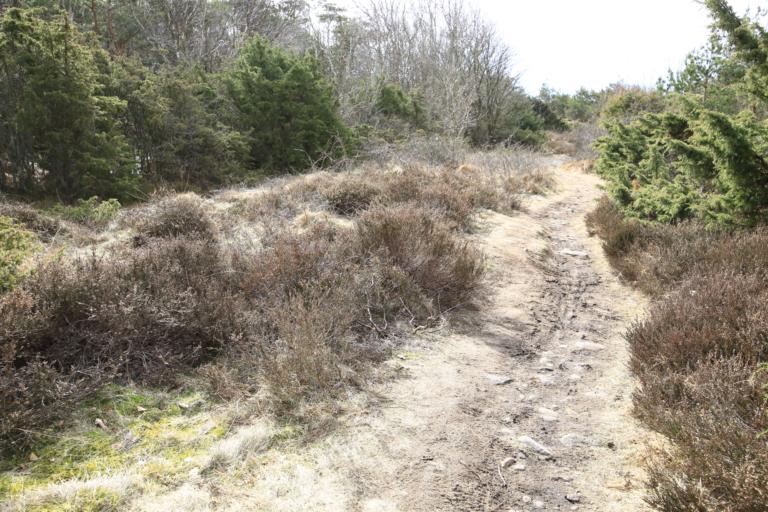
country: SE
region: Halland
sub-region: Kungsbacka Kommun
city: Frillesas
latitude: 57.2345
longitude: 12.1009
